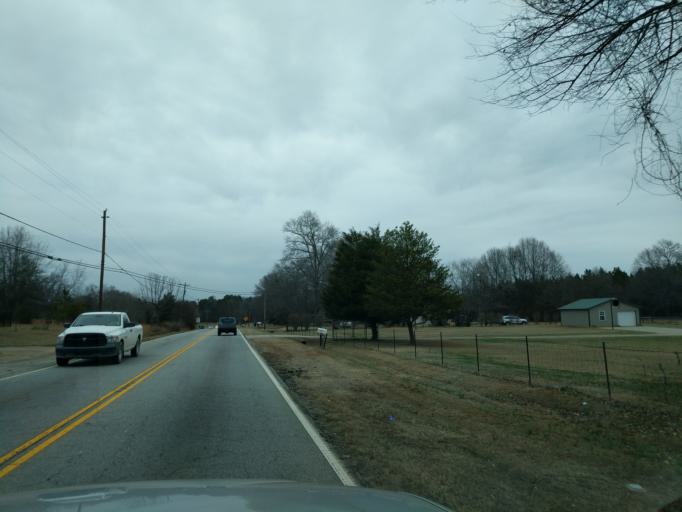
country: US
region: South Carolina
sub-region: Greenville County
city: Taylors
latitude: 34.9776
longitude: -82.3319
